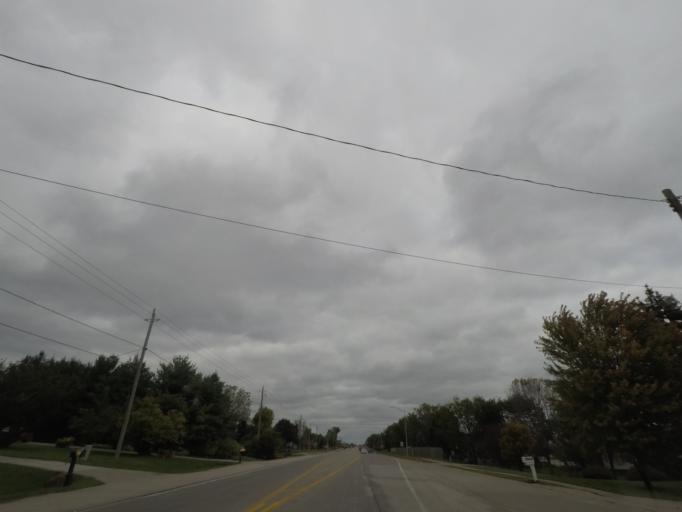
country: US
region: Iowa
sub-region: Polk County
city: Saylorville
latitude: 41.6939
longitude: -93.6006
